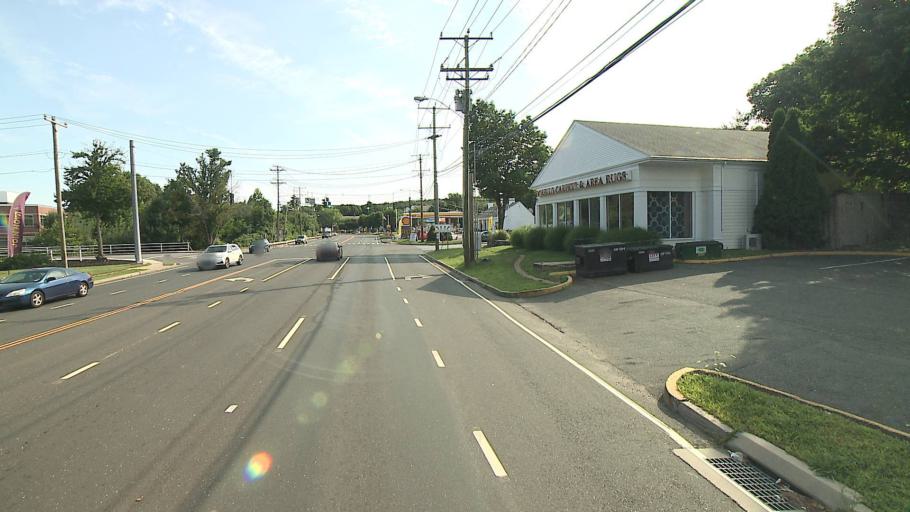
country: US
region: Connecticut
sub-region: Fairfield County
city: Wilton
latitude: 41.1580
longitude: -73.4209
